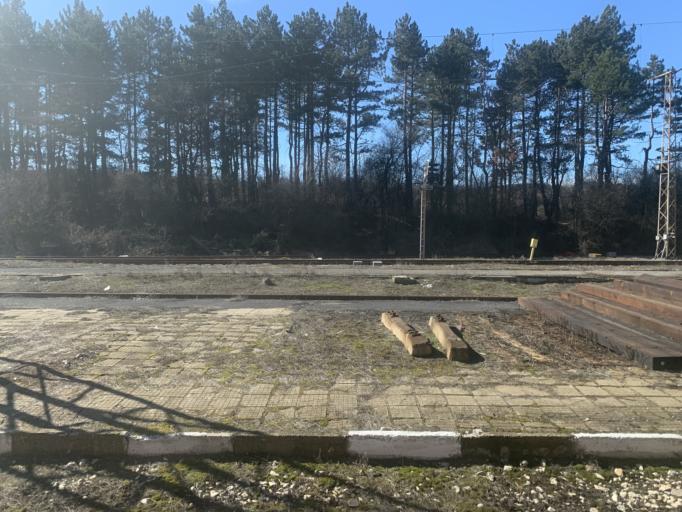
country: BG
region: Sofiya
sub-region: Obshtina Gorna Malina
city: Gorna Malina
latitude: 42.5564
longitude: 23.7072
